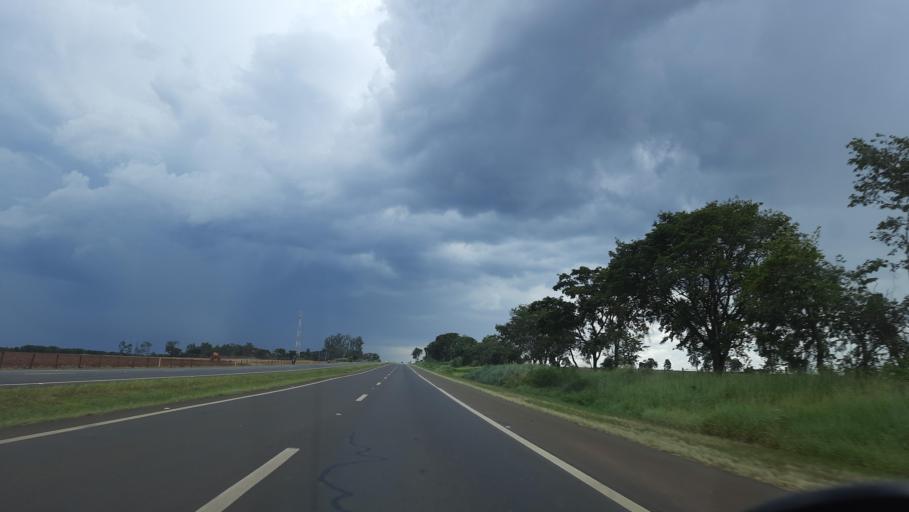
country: BR
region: Sao Paulo
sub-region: Aguai
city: Aguai
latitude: -22.0297
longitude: -47.0331
